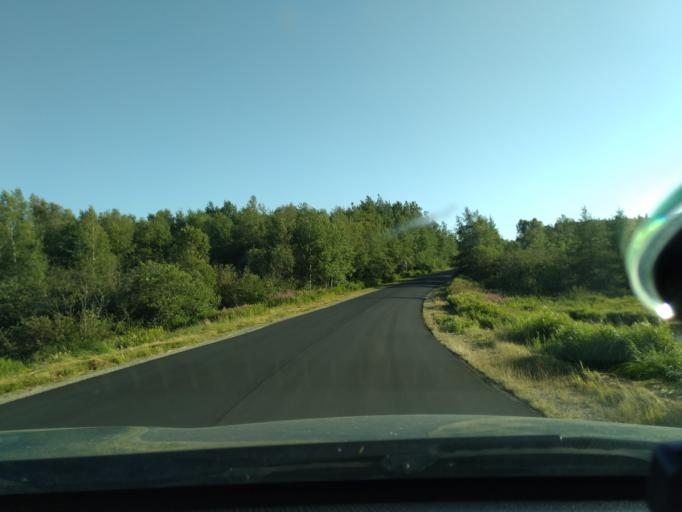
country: US
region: Maine
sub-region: Washington County
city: Eastport
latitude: 44.7186
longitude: -67.1352
